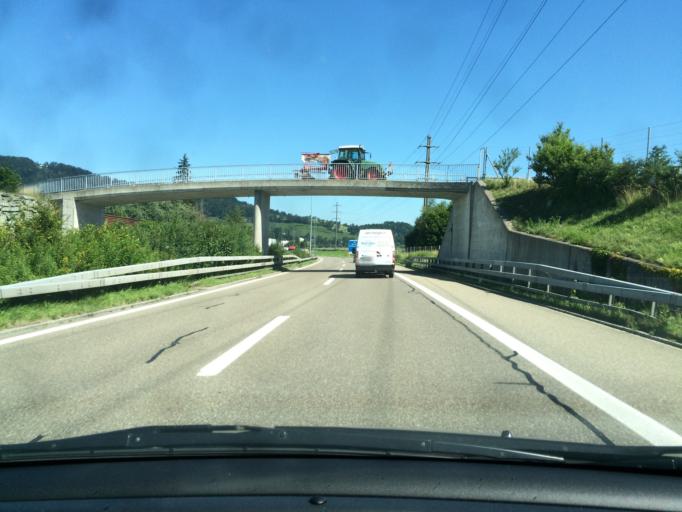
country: AT
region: Vorarlberg
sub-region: Politischer Bezirk Dornbirn
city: Lustenau
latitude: 47.4248
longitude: 9.6463
